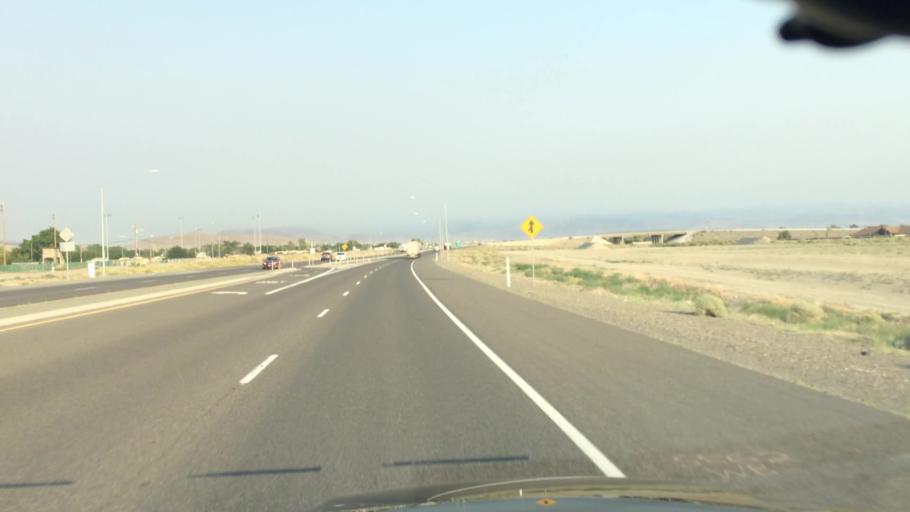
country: US
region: Nevada
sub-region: Lyon County
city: Fernley
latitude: 39.6013
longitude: -119.2184
